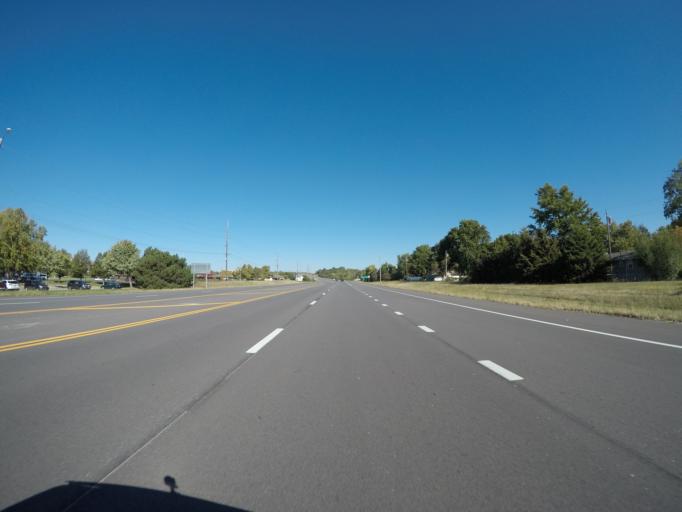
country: US
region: Kansas
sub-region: Riley County
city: Manhattan
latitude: 39.2086
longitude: -96.6170
